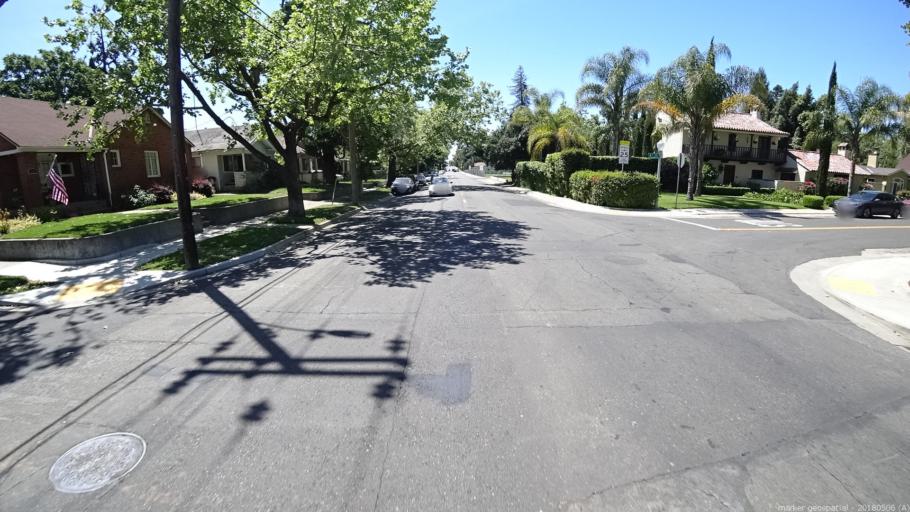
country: US
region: California
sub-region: Sacramento County
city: Sacramento
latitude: 38.5461
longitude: -121.4758
